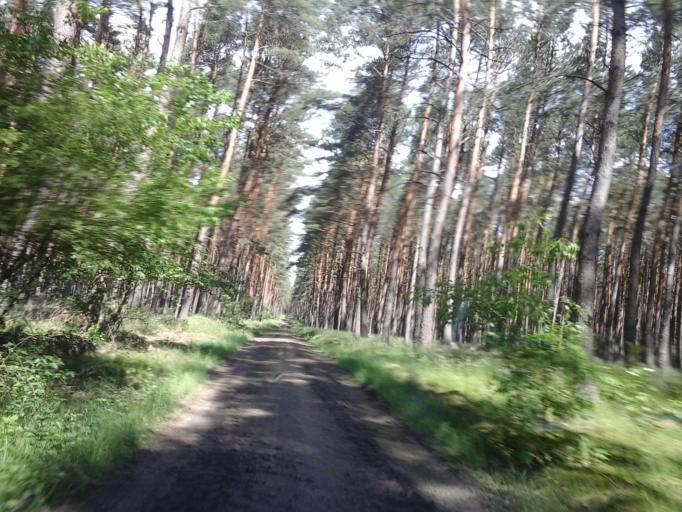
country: PL
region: West Pomeranian Voivodeship
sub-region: Powiat choszczenski
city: Bierzwnik
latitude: 53.1104
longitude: 15.6940
